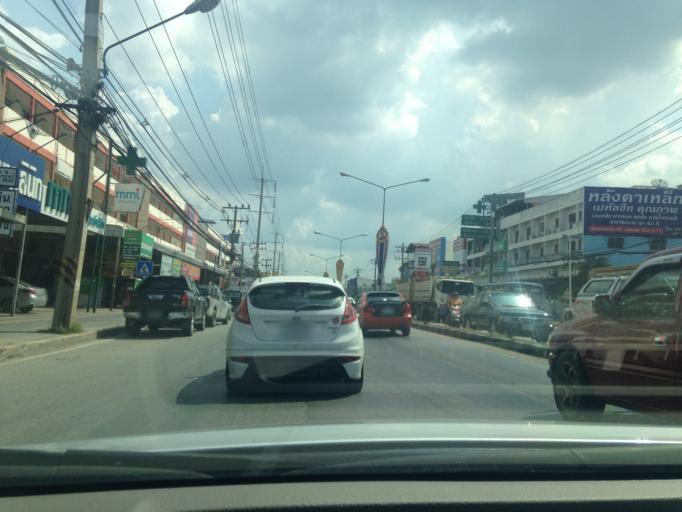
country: TH
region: Pathum Thani
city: Sam Khok
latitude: 14.0440
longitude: 100.5253
